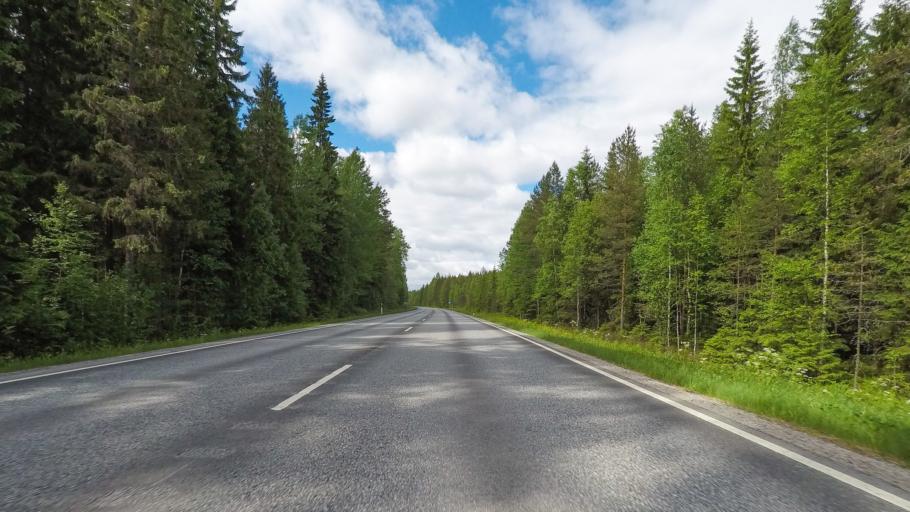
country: FI
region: Central Finland
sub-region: Jyvaeskylae
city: Toivakka
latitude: 62.2233
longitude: 26.2016
